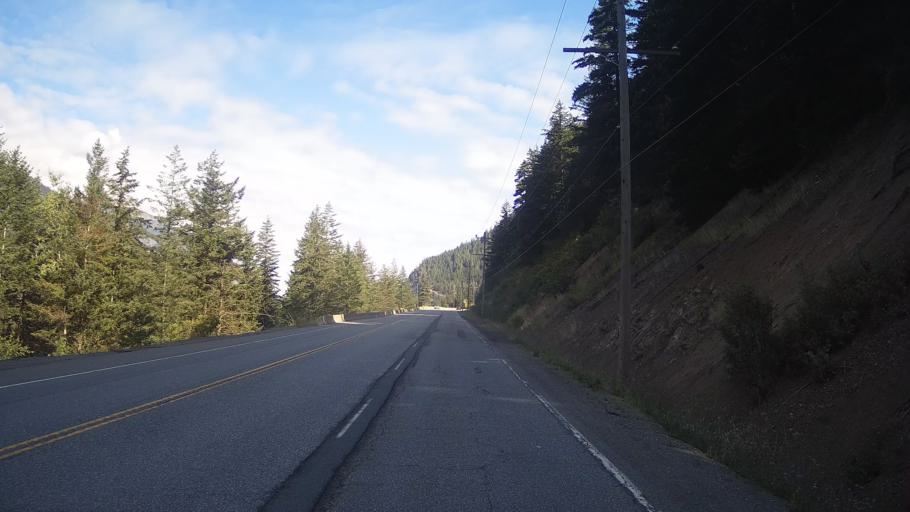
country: CA
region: British Columbia
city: Hope
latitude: 50.0597
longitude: -121.5436
